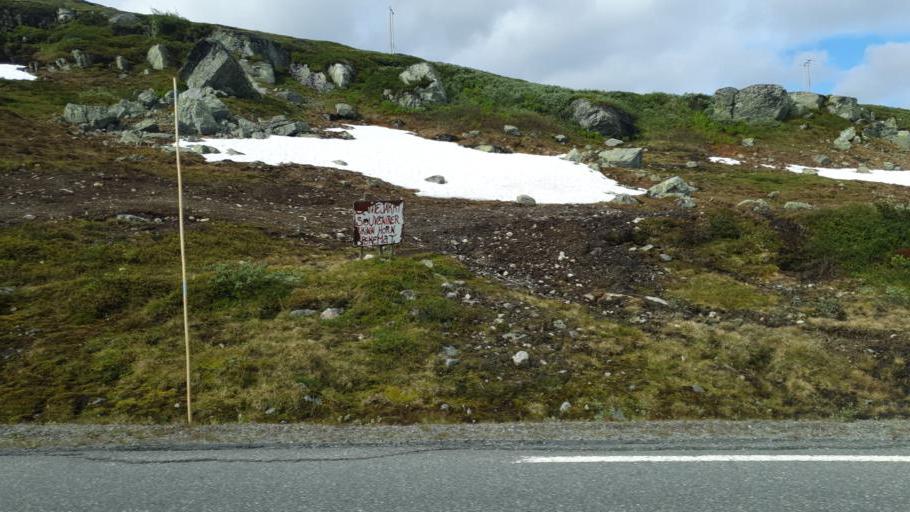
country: NO
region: Oppland
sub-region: Vestre Slidre
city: Slidre
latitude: 61.3223
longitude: 8.8034
